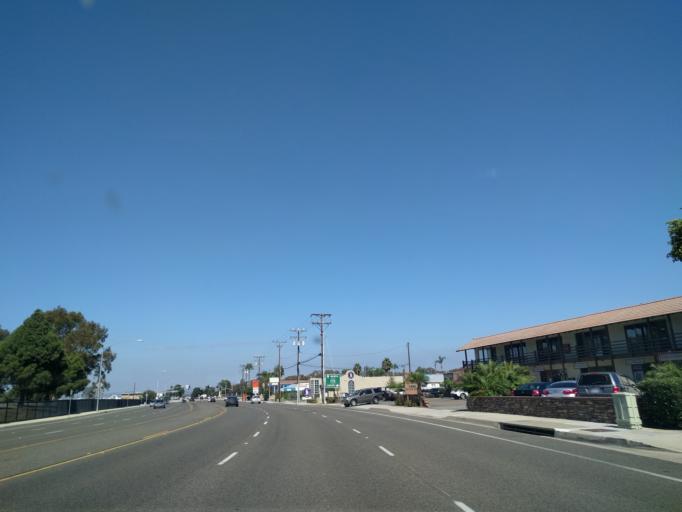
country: US
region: California
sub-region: Orange County
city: Costa Mesa
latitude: 33.6601
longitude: -117.8774
